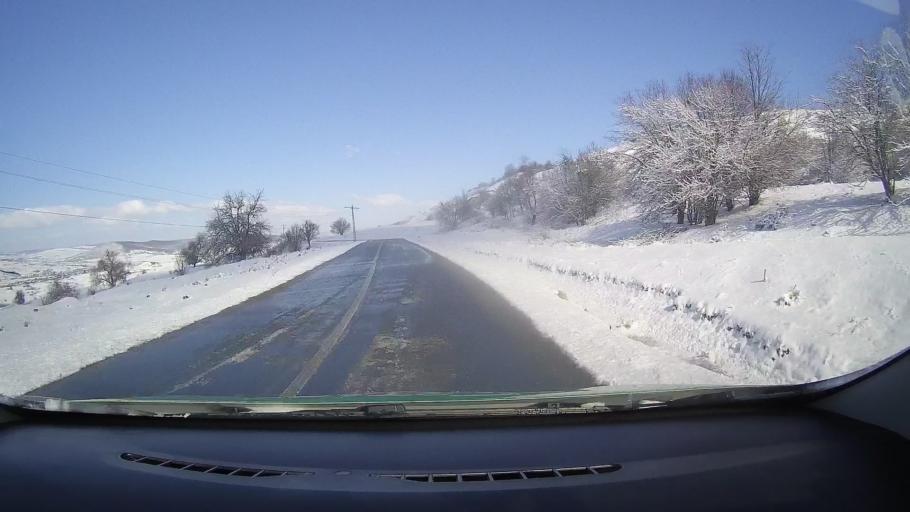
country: RO
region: Sibiu
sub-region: Comuna Avrig
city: Avrig
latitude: 45.7829
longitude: 24.3746
